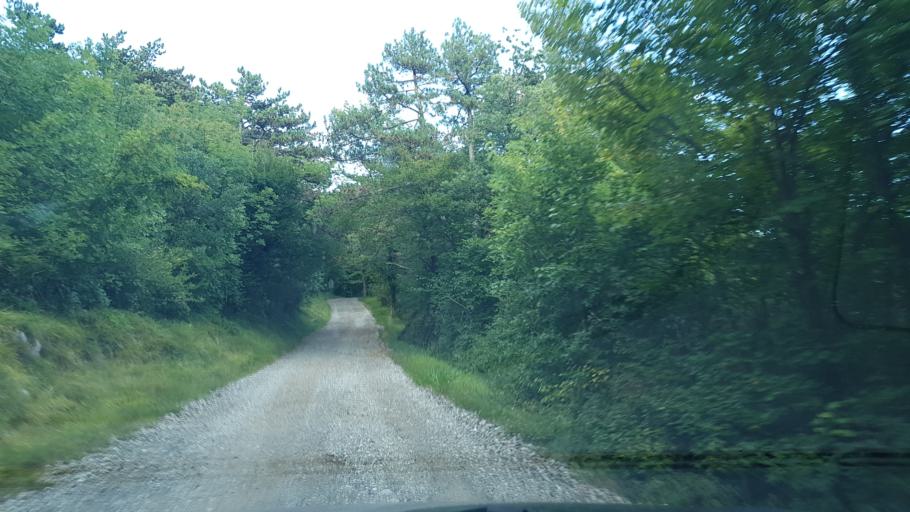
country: SI
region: Nova Gorica
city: Prvacina
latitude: 45.8556
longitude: 13.7046
